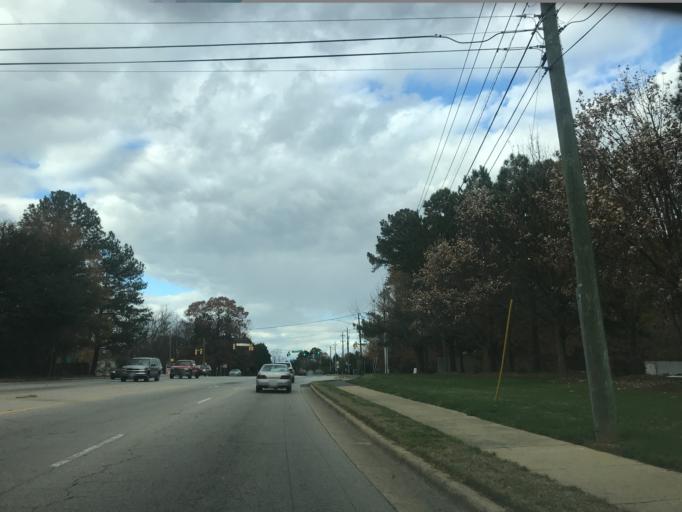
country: US
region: North Carolina
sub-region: Wake County
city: Raleigh
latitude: 35.8051
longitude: -78.5646
